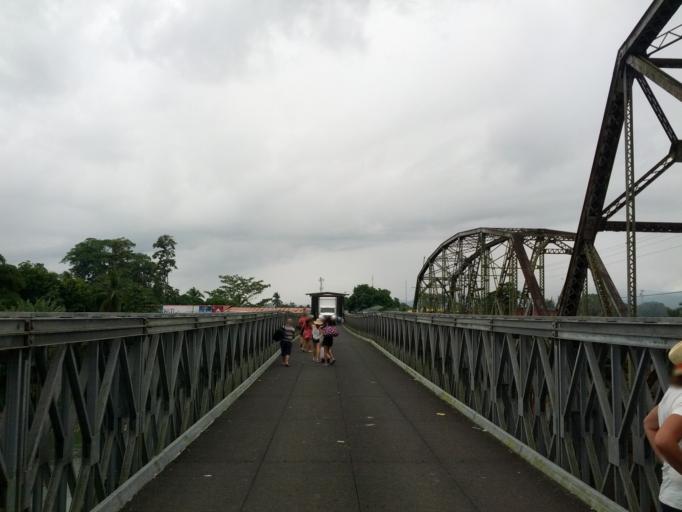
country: PA
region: Bocas del Toro
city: Guabito
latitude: 9.4996
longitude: -82.6136
